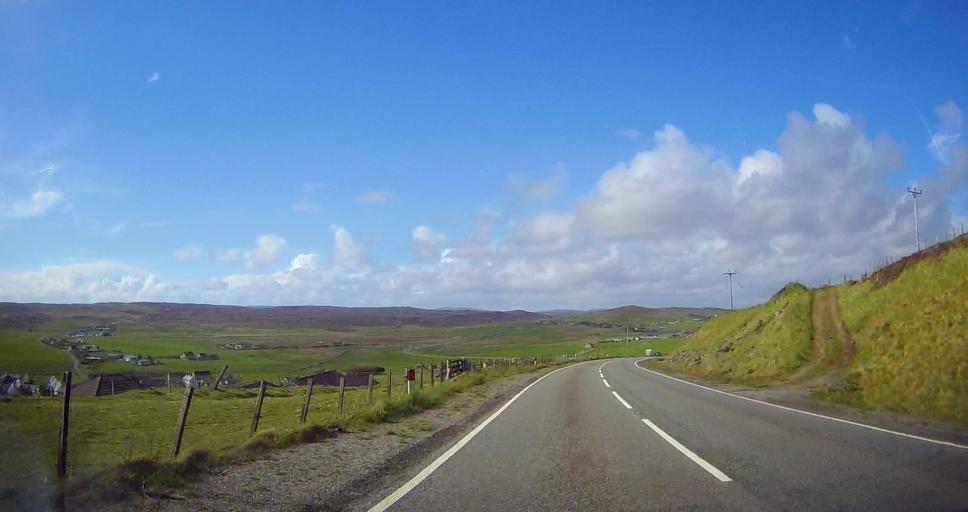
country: GB
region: Scotland
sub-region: Shetland Islands
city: Lerwick
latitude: 60.1799
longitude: -1.2246
